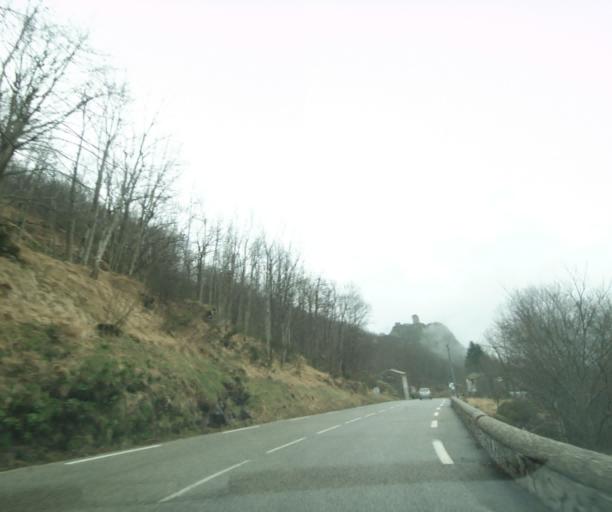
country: FR
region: Rhone-Alpes
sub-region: Departement de l'Ardeche
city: Thueyts
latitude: 44.6768
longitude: 4.0981
